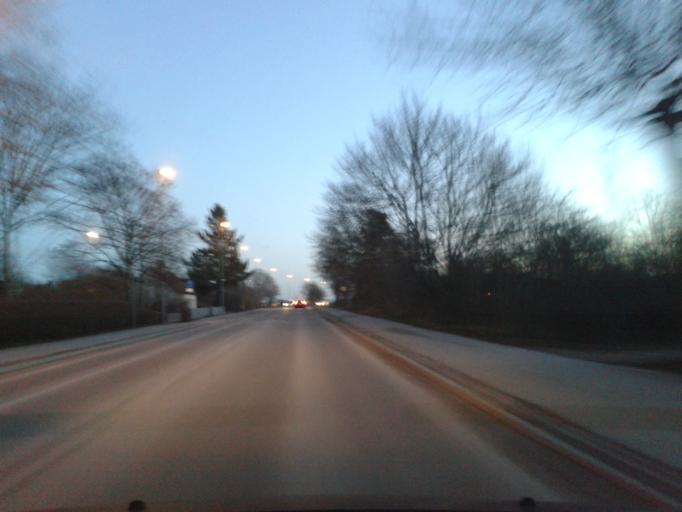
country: SE
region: Gotland
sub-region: Gotland
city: Visby
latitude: 57.6295
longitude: 18.3155
